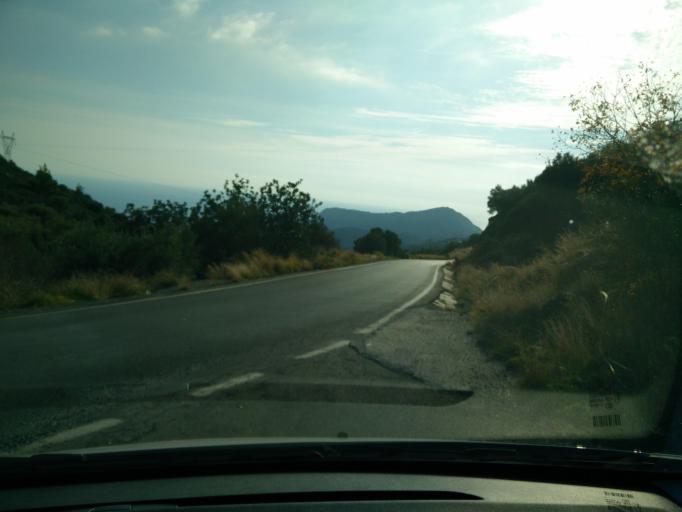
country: GR
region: Crete
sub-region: Nomos Lasithiou
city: Gra Liyia
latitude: 35.0245
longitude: 25.5605
